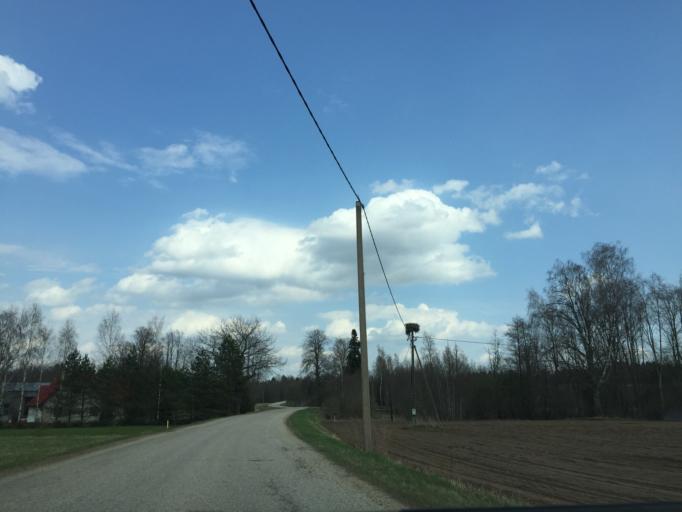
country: RU
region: Pskov
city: Pechory
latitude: 57.7187
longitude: 27.3295
